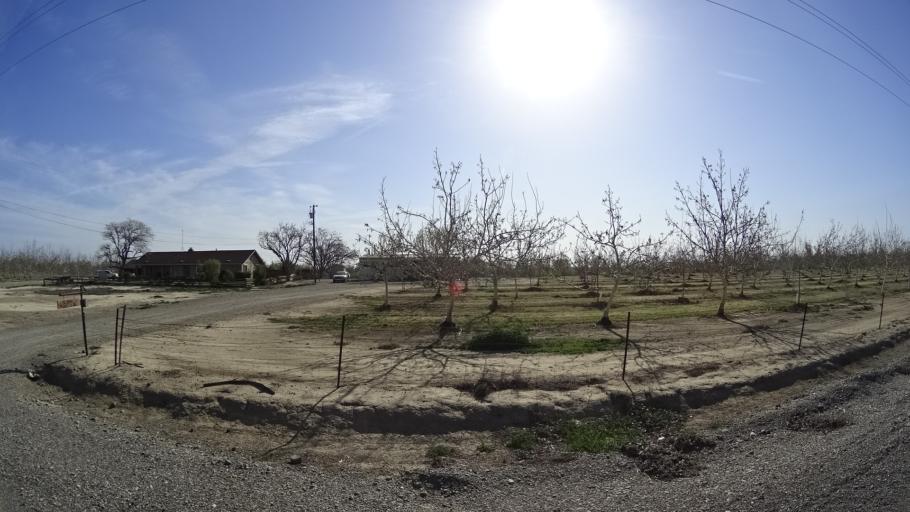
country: US
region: California
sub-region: Glenn County
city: Willows
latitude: 39.5512
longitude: -122.1651
